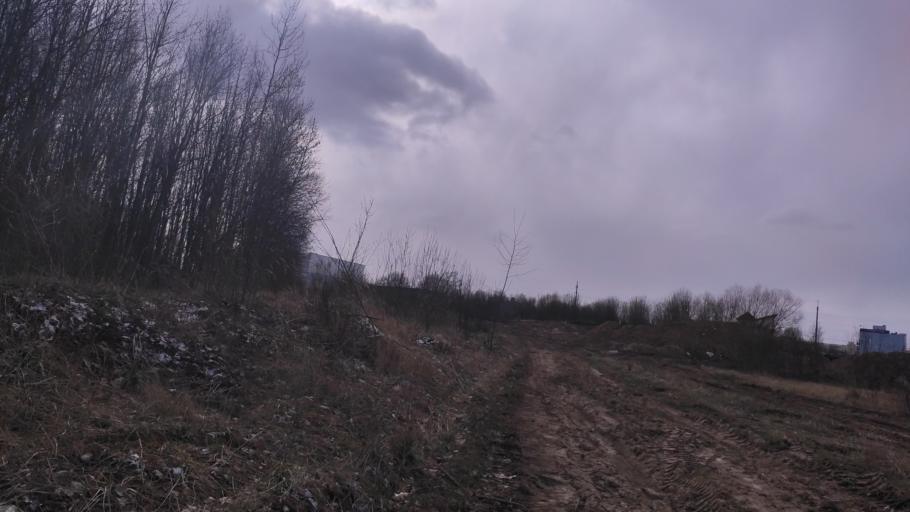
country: BY
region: Minsk
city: Novoye Medvezhino
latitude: 53.8925
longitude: 27.4681
